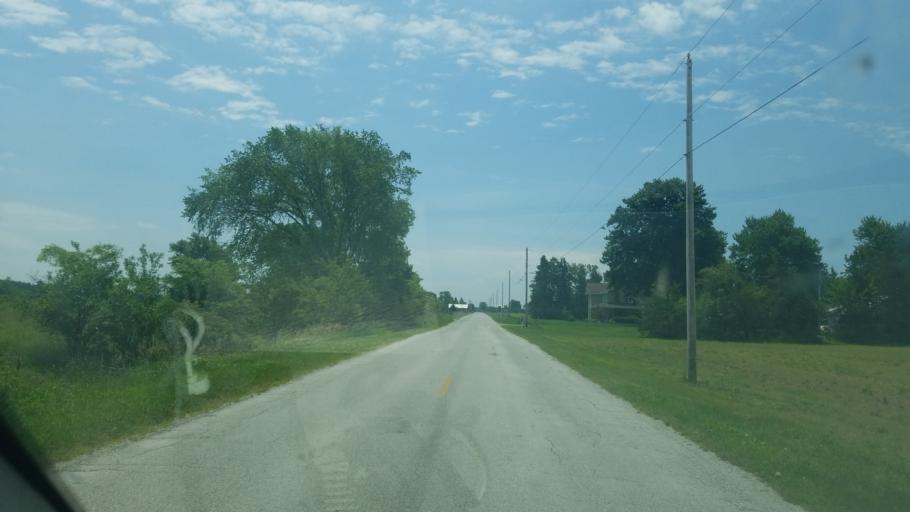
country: US
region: Ohio
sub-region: Wood County
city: North Baltimore
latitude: 41.2164
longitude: -83.5924
